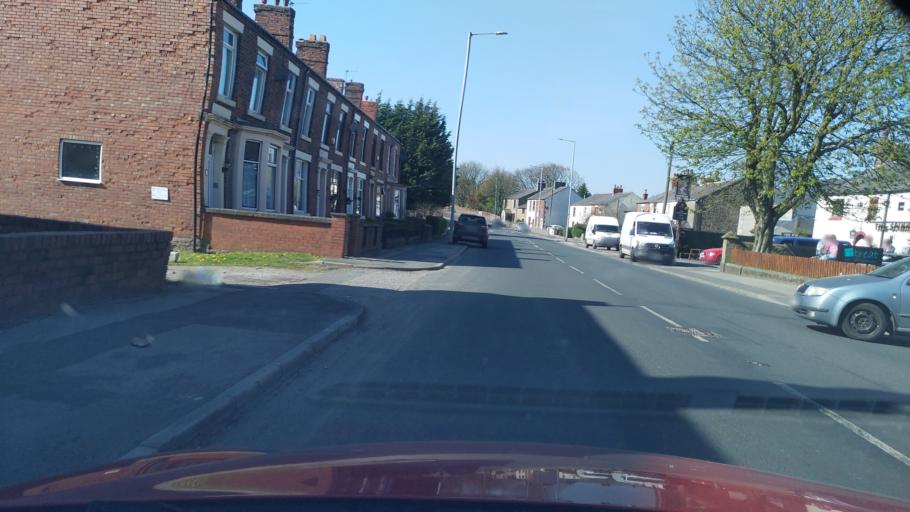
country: GB
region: England
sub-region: Lancashire
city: Adlington
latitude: 53.6135
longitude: -2.6049
